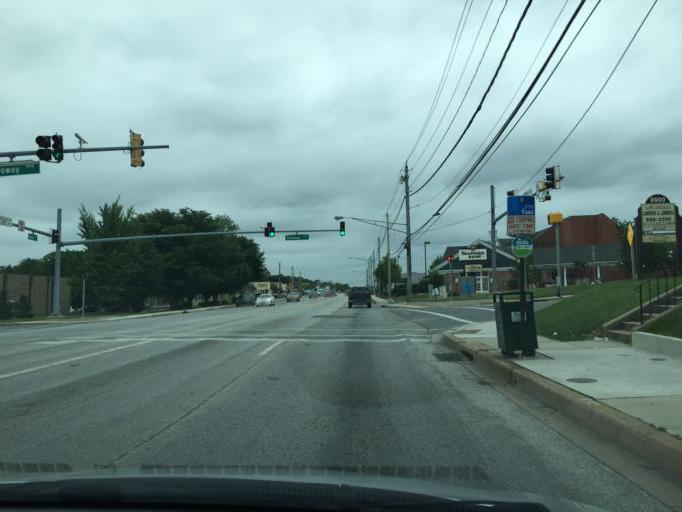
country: US
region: Maryland
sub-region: Baltimore County
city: Cockeysville
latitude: 39.4610
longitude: -76.6352
